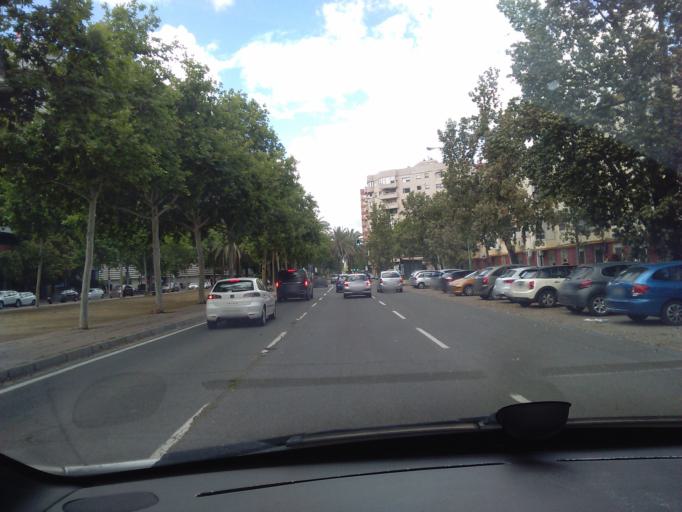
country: ES
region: Andalusia
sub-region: Provincia de Sevilla
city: Sevilla
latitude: 37.3734
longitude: -5.9763
